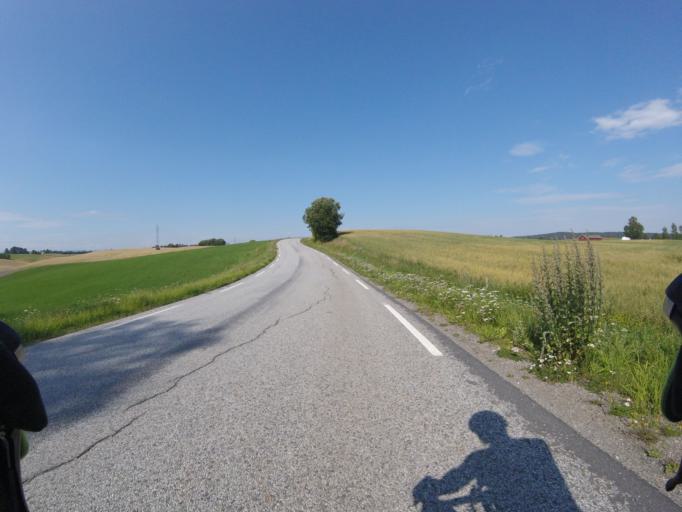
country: NO
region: Akershus
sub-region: Ullensaker
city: Klofta
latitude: 60.0950
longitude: 11.1612
